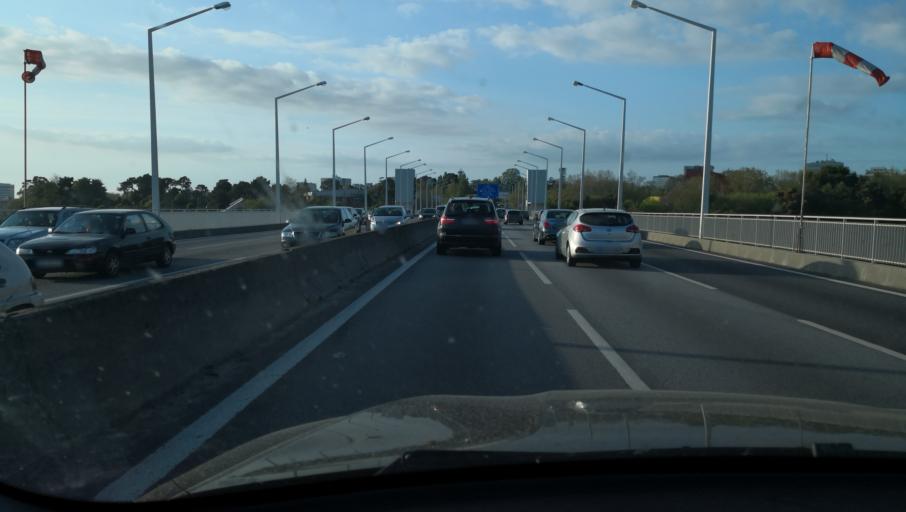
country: PT
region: Porto
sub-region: Vila Nova de Gaia
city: Canidelo
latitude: 41.1472
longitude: -8.6402
